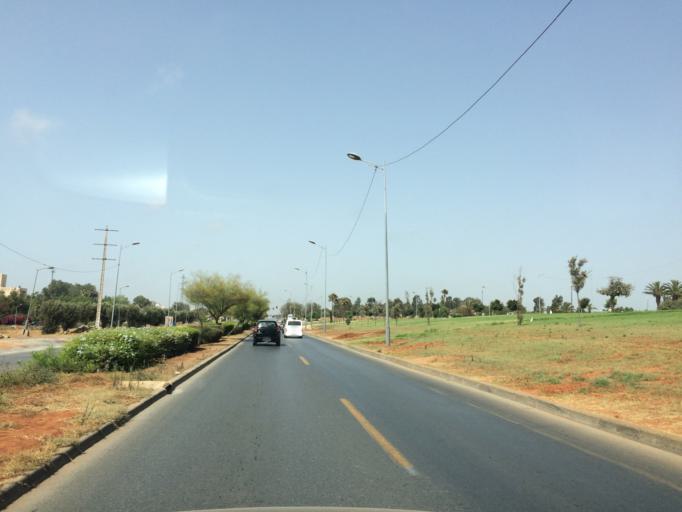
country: MA
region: Rabat-Sale-Zemmour-Zaer
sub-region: Rabat
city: Rabat
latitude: 33.9744
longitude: -6.8636
